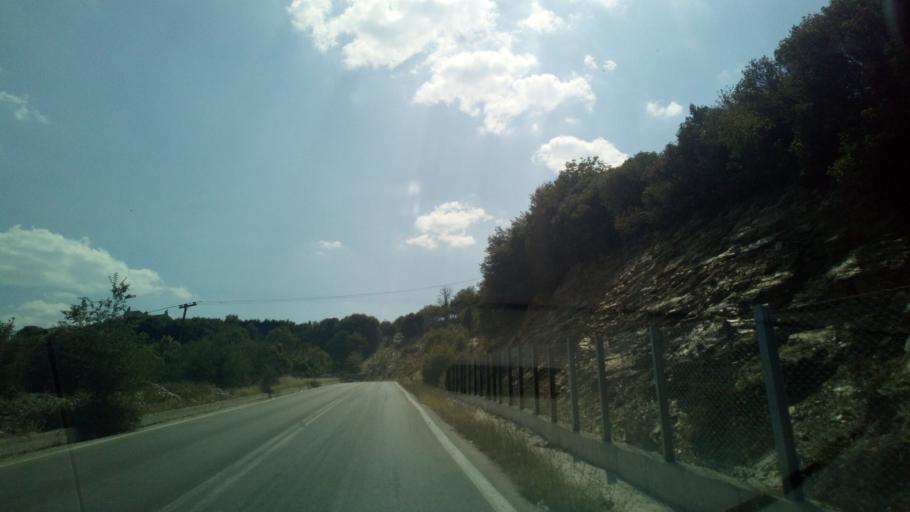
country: GR
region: Central Macedonia
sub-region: Nomos Thessalonikis
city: Chortiatis
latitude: 40.6329
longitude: 23.0991
